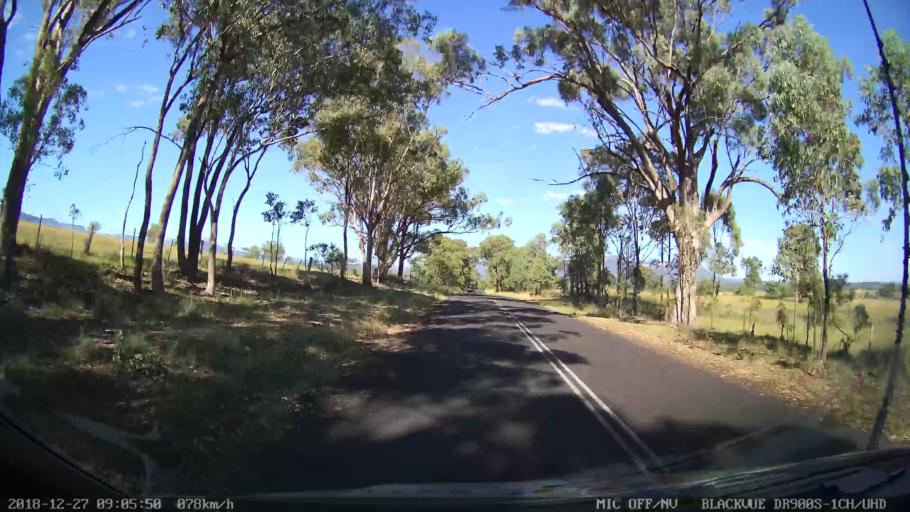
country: AU
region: New South Wales
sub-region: Lithgow
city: Portland
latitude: -33.1196
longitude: 150.1753
